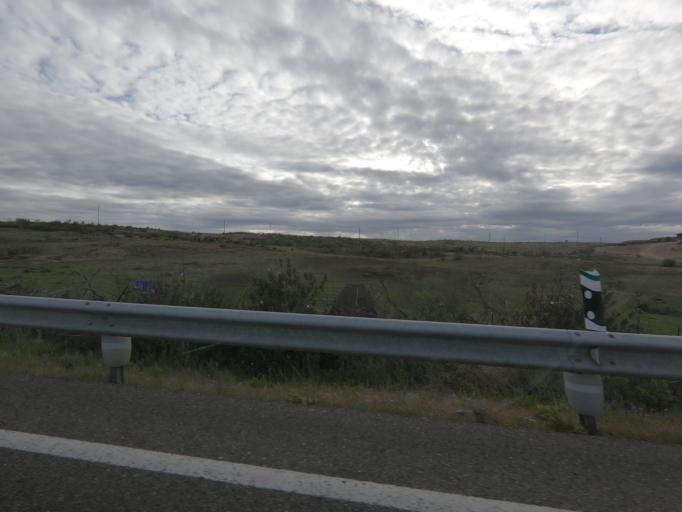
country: ES
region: Extremadura
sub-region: Provincia de Caceres
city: Coria
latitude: 39.9395
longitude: -6.5066
